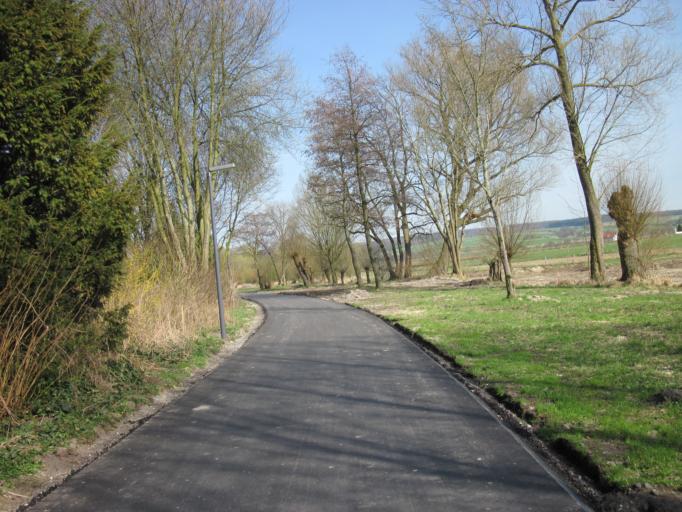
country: DE
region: North Rhine-Westphalia
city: Bad Lippspringe
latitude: 51.7905
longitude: 8.8340
